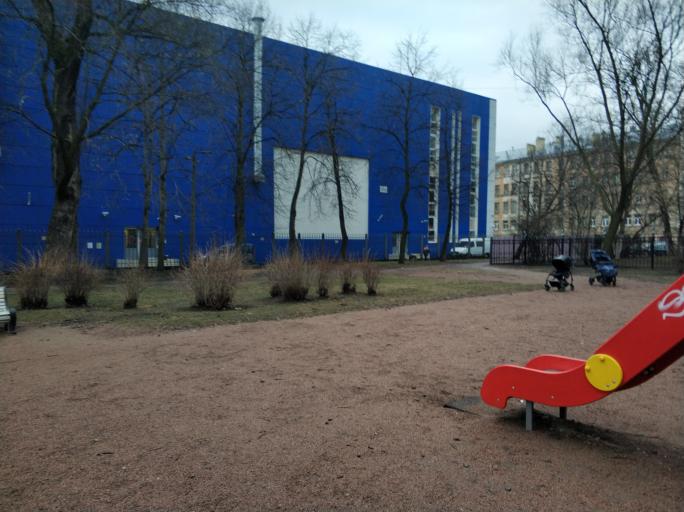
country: RU
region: Leningrad
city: Finlyandskiy
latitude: 59.9680
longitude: 30.3480
